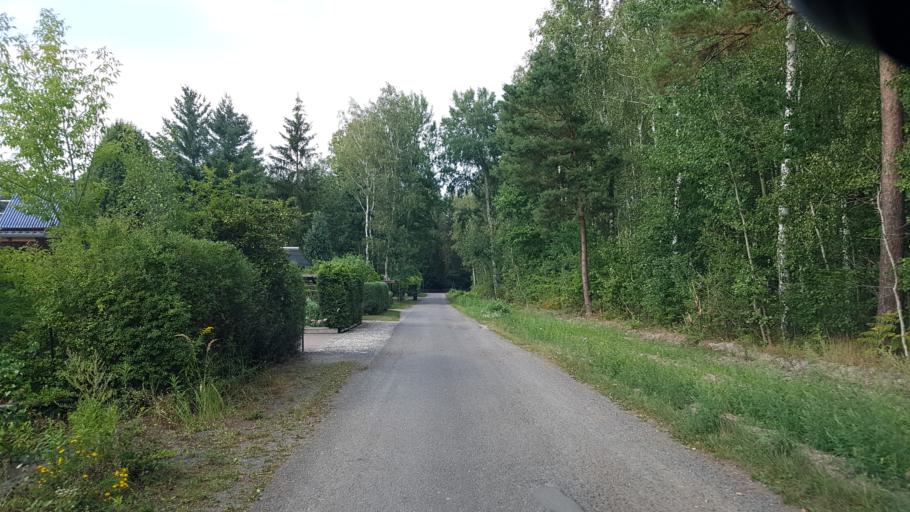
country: DE
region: Brandenburg
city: Plessa
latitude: 51.5151
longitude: 13.6693
